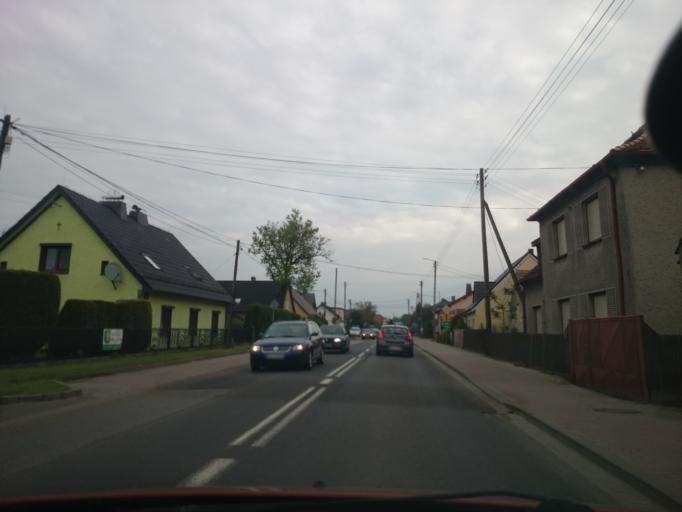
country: PL
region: Opole Voivodeship
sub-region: Powiat opolski
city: Dobrzen Wielki
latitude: 50.7692
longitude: 17.8492
